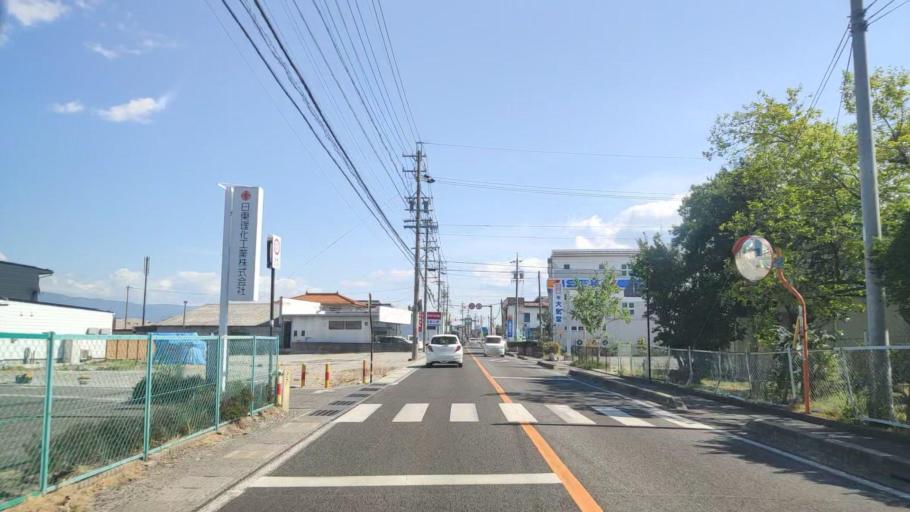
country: JP
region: Nagano
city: Toyoshina
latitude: 36.2896
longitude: 137.9073
